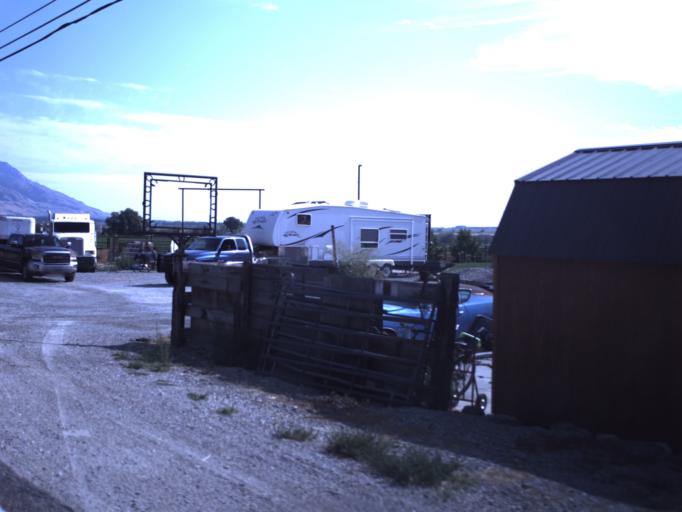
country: US
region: Utah
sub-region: Box Elder County
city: Honeyville
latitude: 41.5822
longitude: -112.0372
